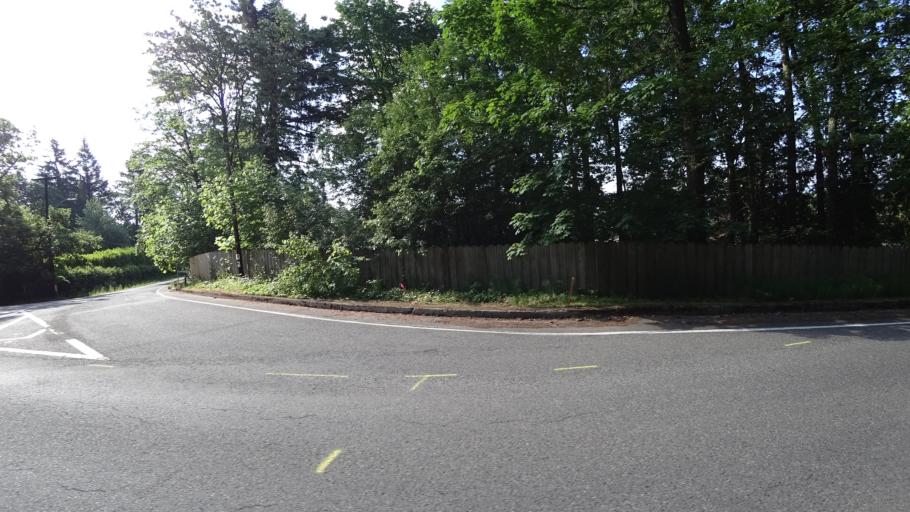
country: US
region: Oregon
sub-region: Washington County
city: West Slope
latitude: 45.4981
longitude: -122.7272
